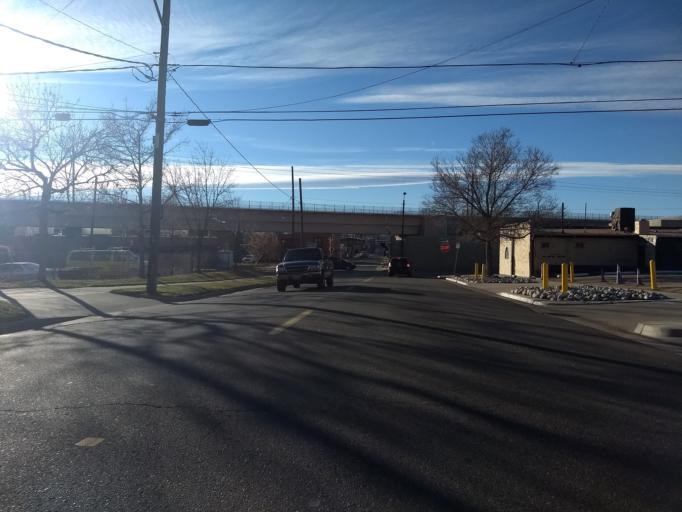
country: US
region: Colorado
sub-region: Denver County
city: Denver
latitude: 39.7184
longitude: -104.9979
